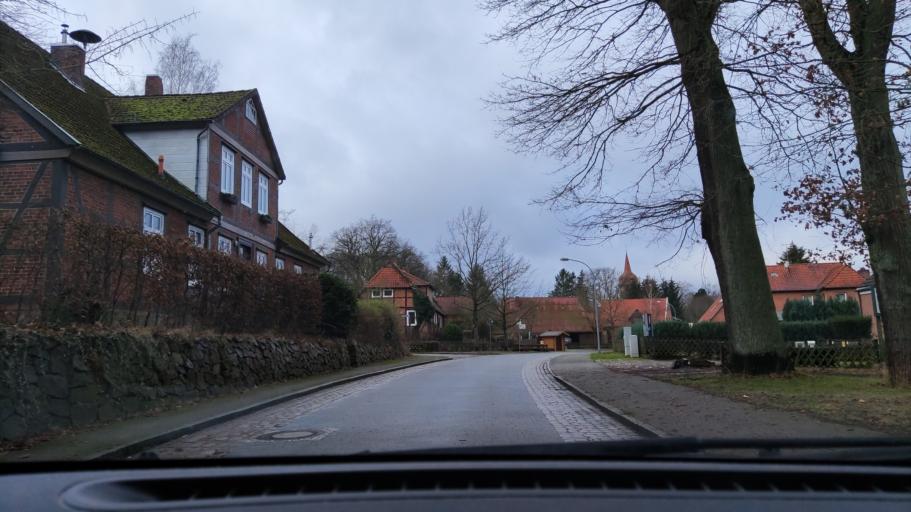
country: DE
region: Lower Saxony
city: Natendorf
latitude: 53.0799
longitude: 10.4697
